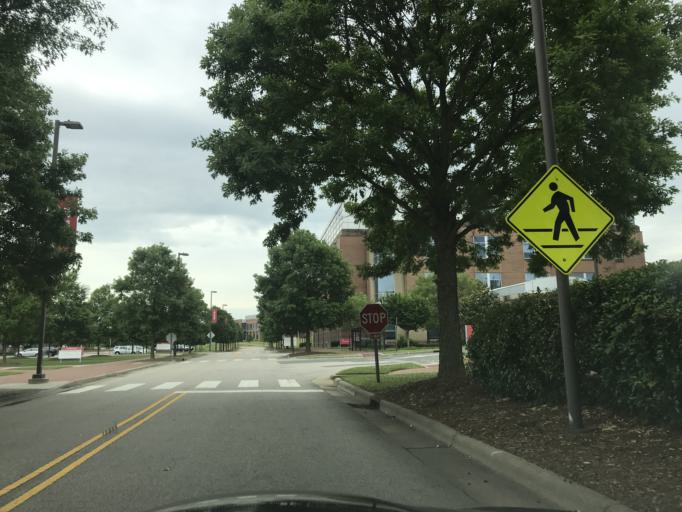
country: US
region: North Carolina
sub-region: Wake County
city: West Raleigh
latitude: 35.7981
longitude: -78.7051
